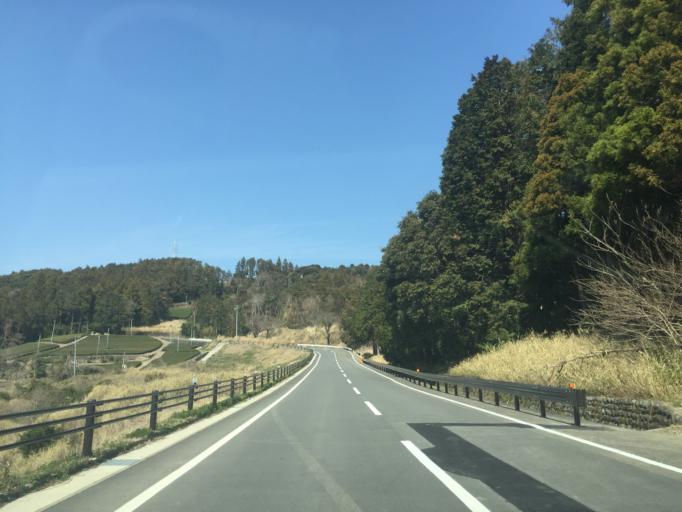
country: JP
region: Shizuoka
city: Kanaya
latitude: 34.8081
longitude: 138.1240
